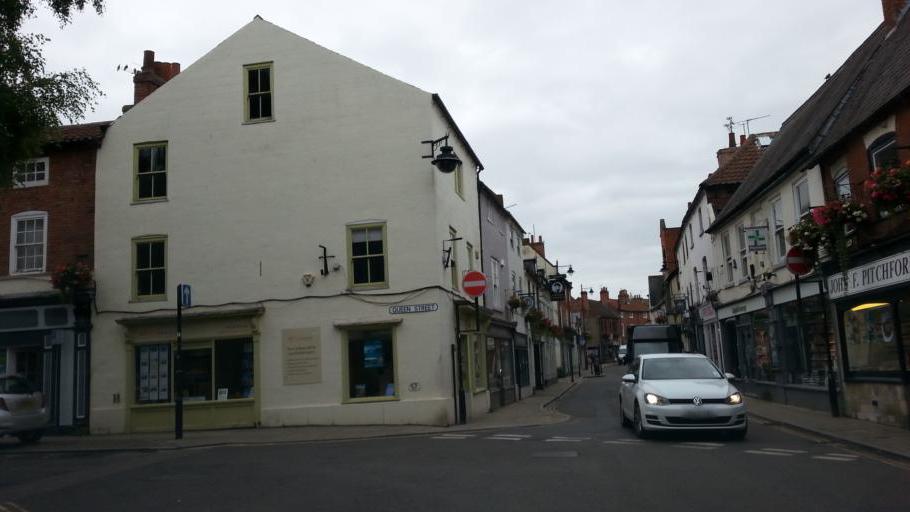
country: GB
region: England
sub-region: Nottinghamshire
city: Southwell
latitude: 53.0782
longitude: -0.9551
